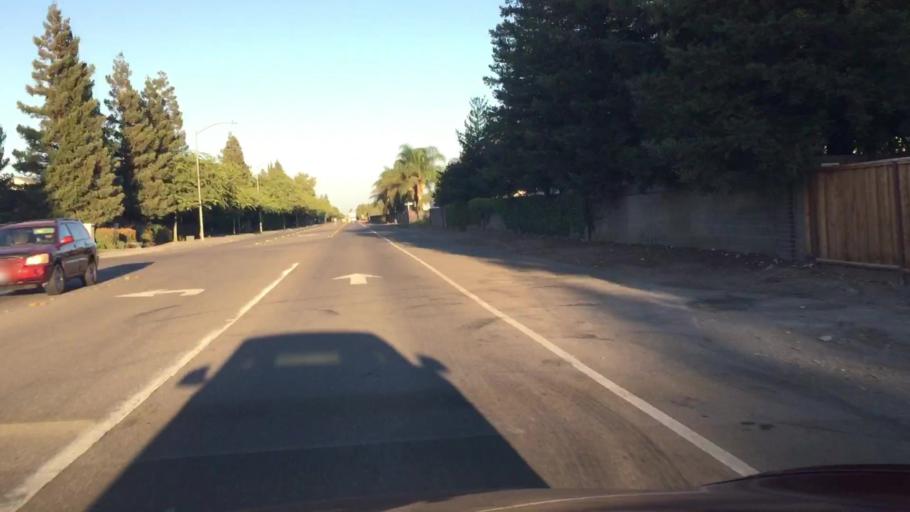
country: US
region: California
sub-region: San Joaquin County
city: Tracy
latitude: 37.7107
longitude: -121.4113
